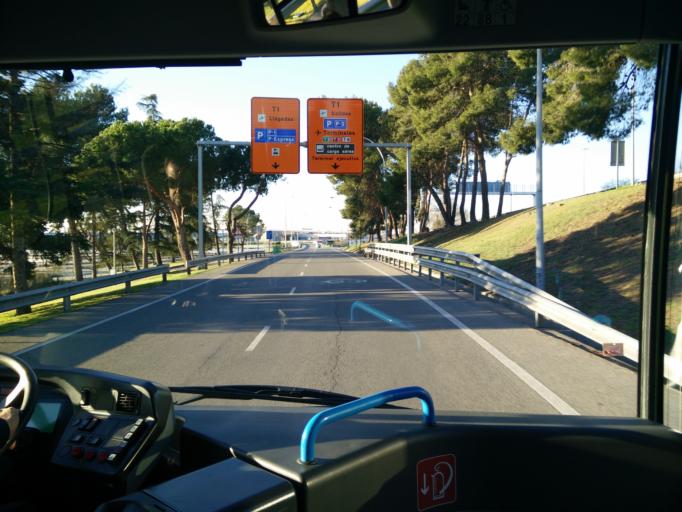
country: ES
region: Madrid
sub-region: Provincia de Madrid
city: Barajas de Madrid
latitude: 40.4653
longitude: -3.5739
